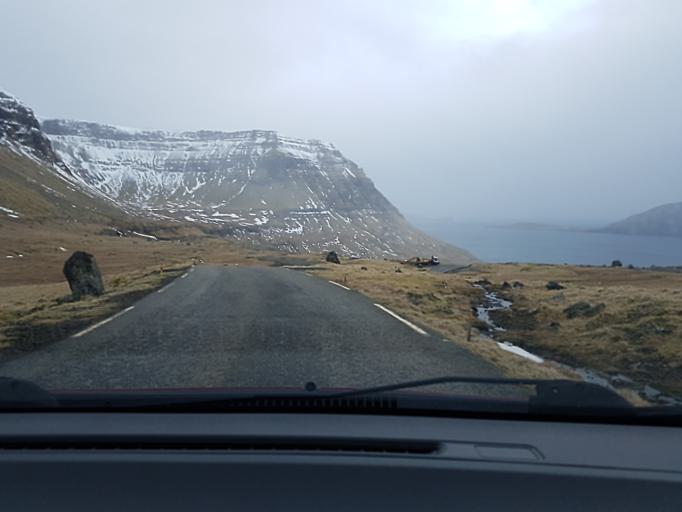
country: FO
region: Streymoy
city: Kollafjordhur
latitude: 62.0525
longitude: -6.9219
